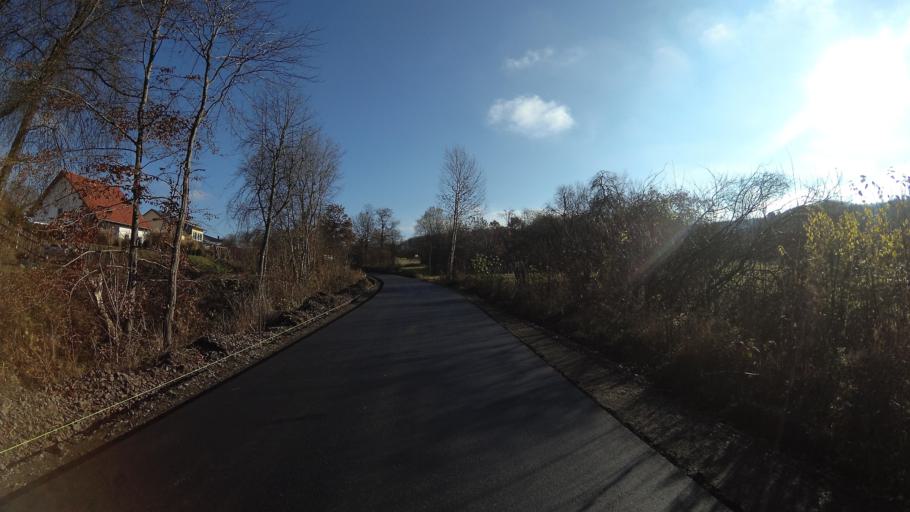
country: DE
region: Saarland
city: Freisen
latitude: 49.5476
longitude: 7.2429
